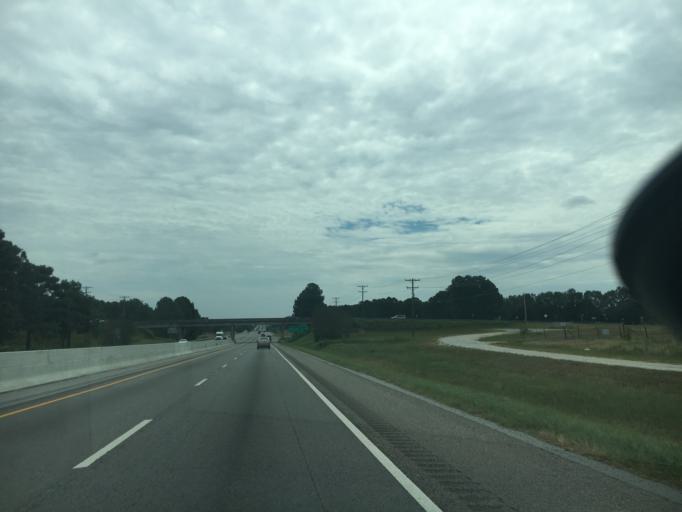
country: US
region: South Carolina
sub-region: Greenville County
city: Fountain Inn
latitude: 34.6894
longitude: -82.2199
